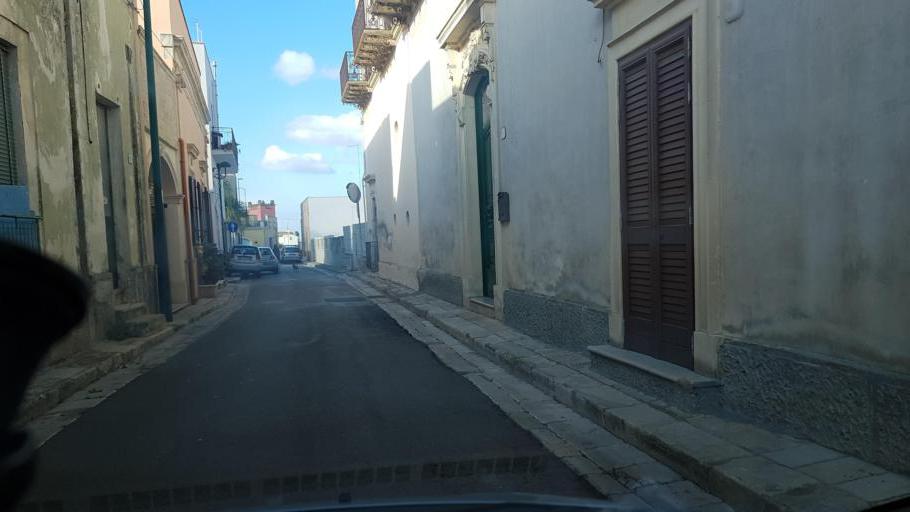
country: IT
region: Apulia
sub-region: Provincia di Lecce
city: Guagnano
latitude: 40.4022
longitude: 17.9524
